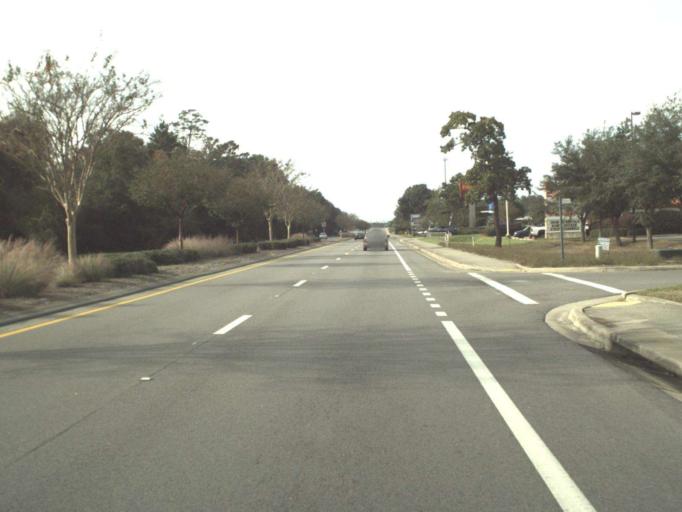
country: US
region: Florida
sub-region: Okaloosa County
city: Niceville
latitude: 30.4848
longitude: -86.4181
